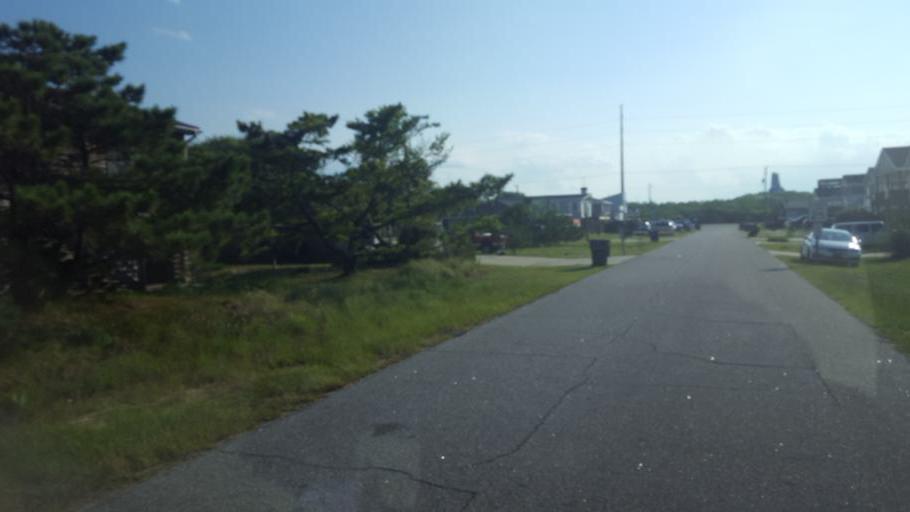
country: US
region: North Carolina
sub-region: Dare County
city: Kill Devil Hills
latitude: 36.0168
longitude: -75.6606
